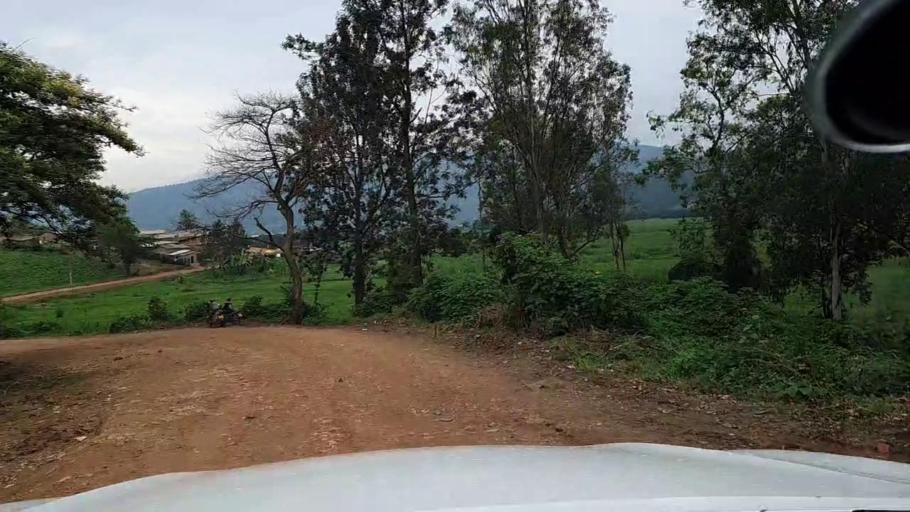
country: RW
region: Kigali
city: Kigali
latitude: -1.9629
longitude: 29.9962
